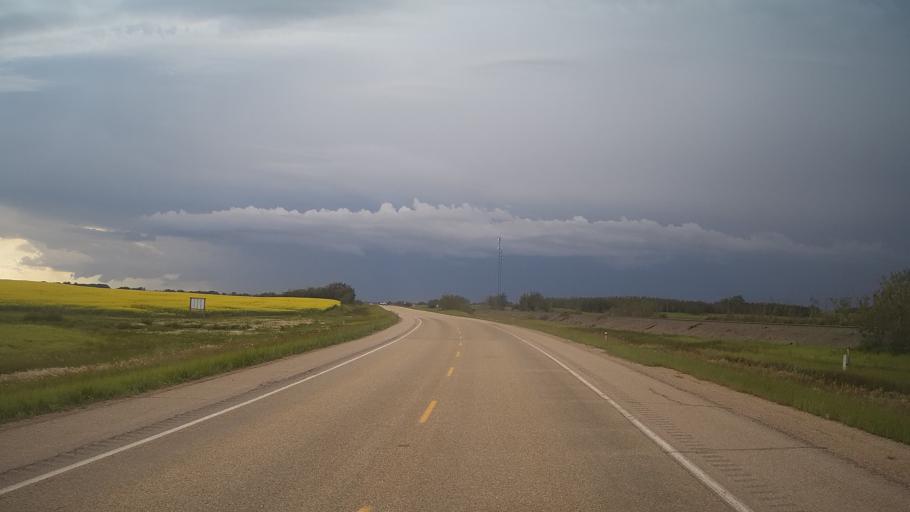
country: CA
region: Alberta
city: Vegreville
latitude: 53.2345
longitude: -112.2515
